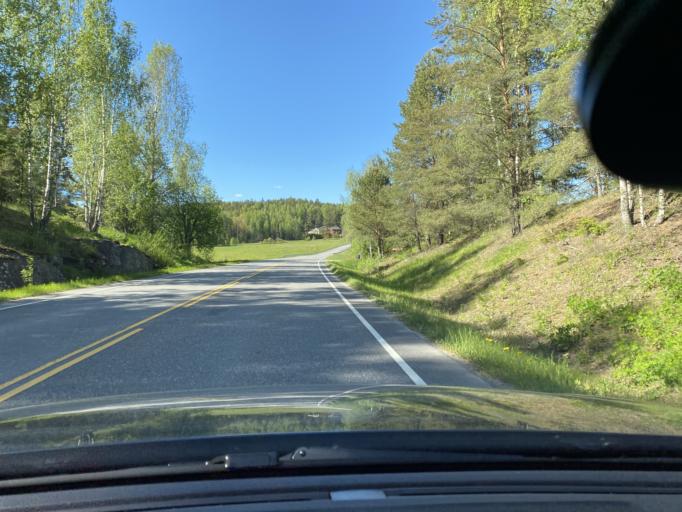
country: FI
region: Varsinais-Suomi
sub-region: Turku
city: Sauvo
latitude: 60.3782
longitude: 22.6671
